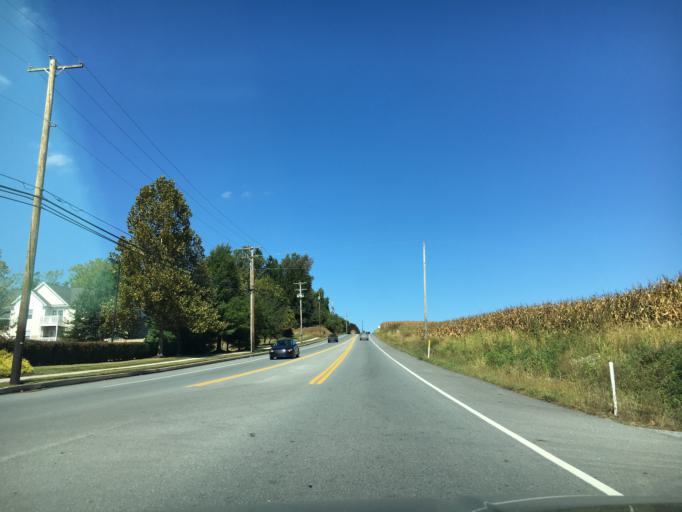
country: US
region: Pennsylvania
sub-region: York County
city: Stonybrook
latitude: 39.9482
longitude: -76.6480
